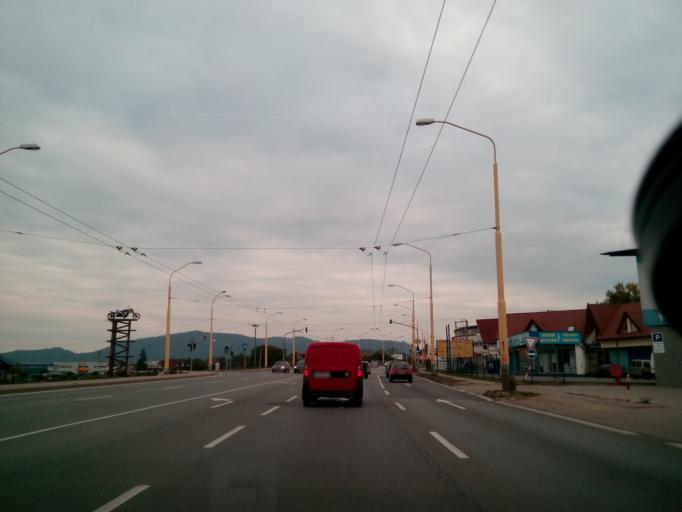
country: SK
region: Presovsky
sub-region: Okres Presov
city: Presov
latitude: 49.0190
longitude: 21.2728
